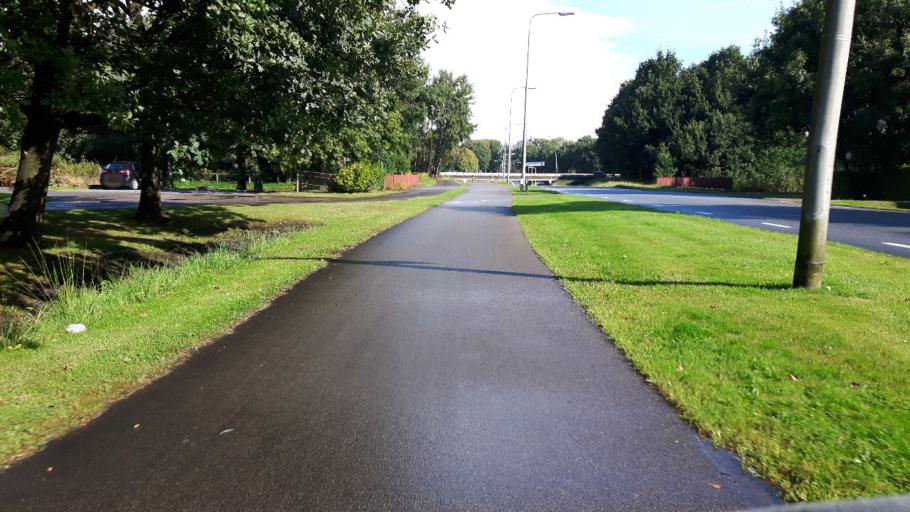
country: NL
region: Friesland
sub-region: Gemeente Smallingerland
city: Drachten
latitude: 53.0916
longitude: 6.0994
